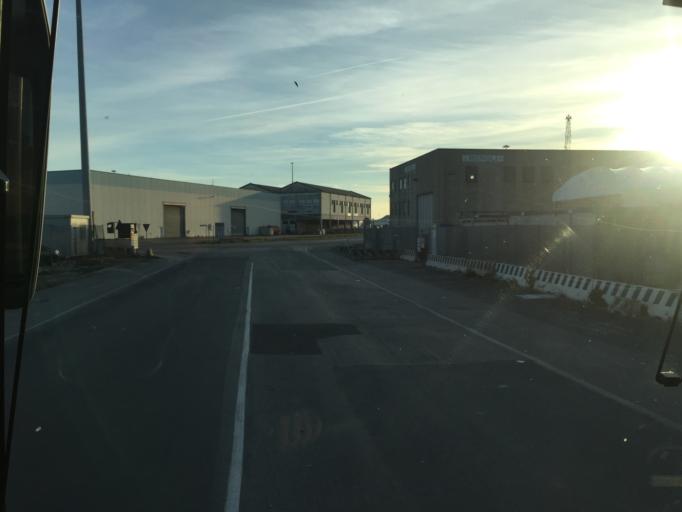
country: IT
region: Tuscany
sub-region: Provincia di Livorno
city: Livorno
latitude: 43.5589
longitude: 10.3025
